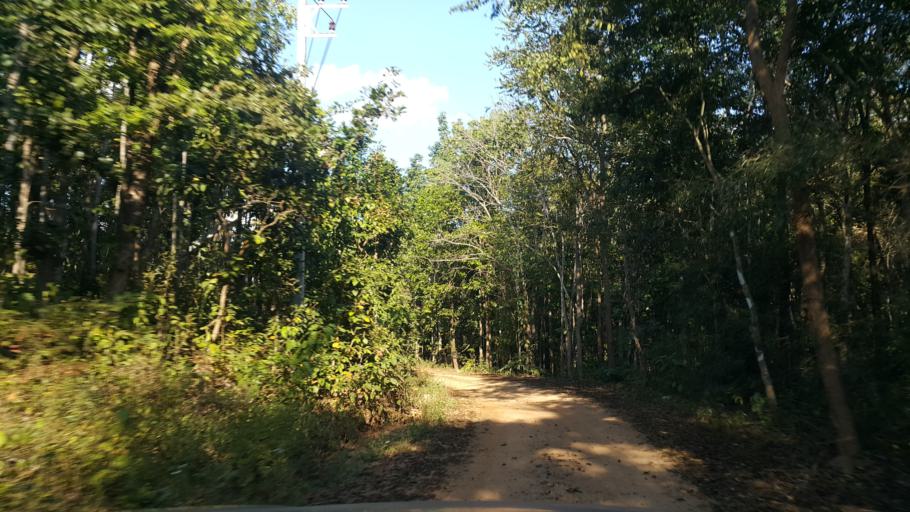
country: TH
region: Lamphun
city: Mae Tha
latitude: 18.5259
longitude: 99.1216
